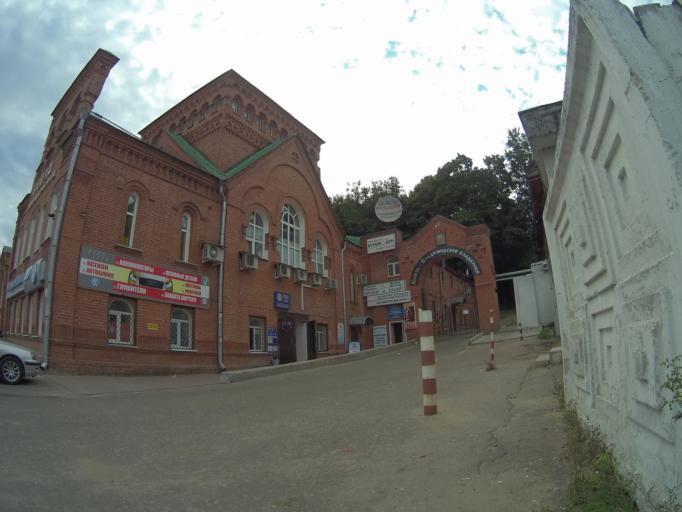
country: RU
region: Vladimir
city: Kommunar
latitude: 56.1419
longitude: 40.4371
